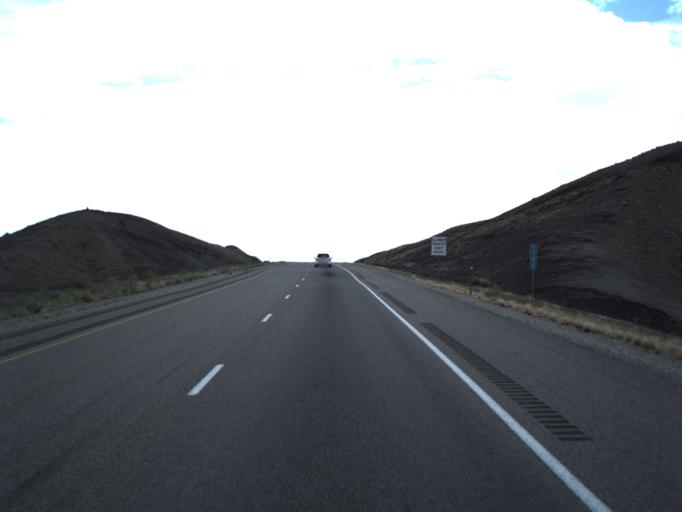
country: US
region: Utah
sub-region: Carbon County
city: East Carbon City
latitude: 38.9699
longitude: -110.0962
